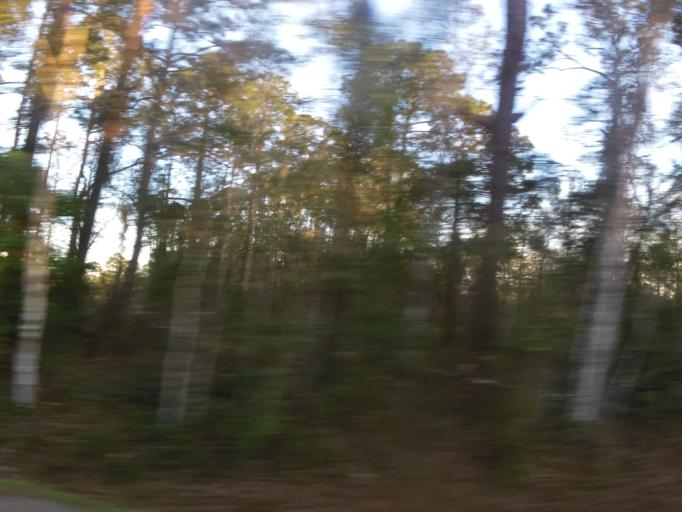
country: US
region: Florida
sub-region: Clay County
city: Green Cove Springs
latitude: 29.9531
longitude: -81.5502
